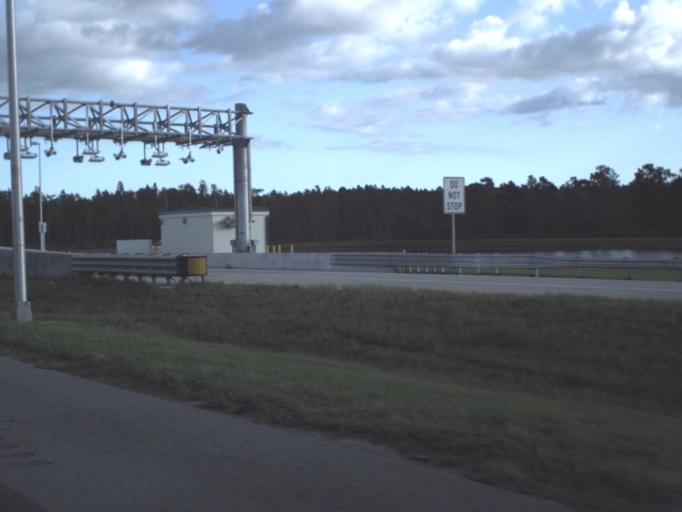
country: US
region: Florida
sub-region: Orange County
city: Southchase
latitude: 28.3745
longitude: -81.3901
